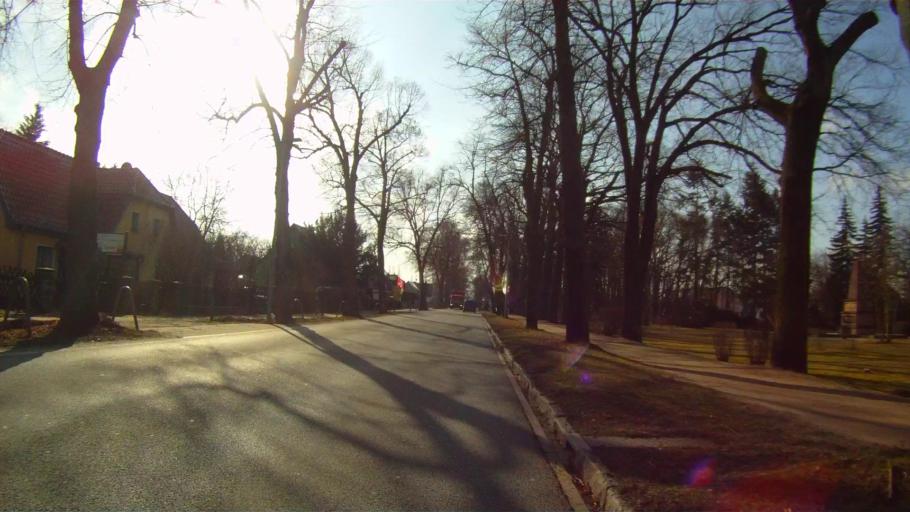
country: DE
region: Brandenburg
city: Erkner
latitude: 52.4155
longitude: 13.7538
